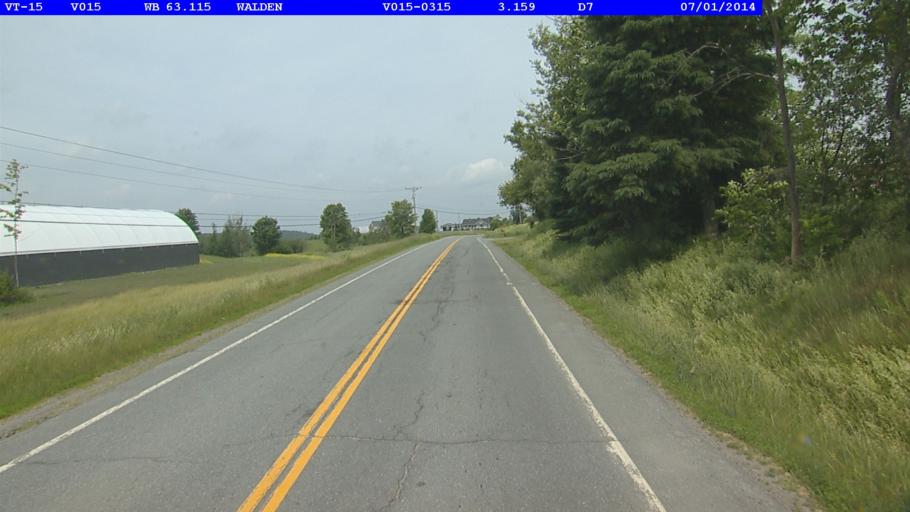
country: US
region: Vermont
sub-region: Caledonia County
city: Hardwick
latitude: 44.4552
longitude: -72.2609
